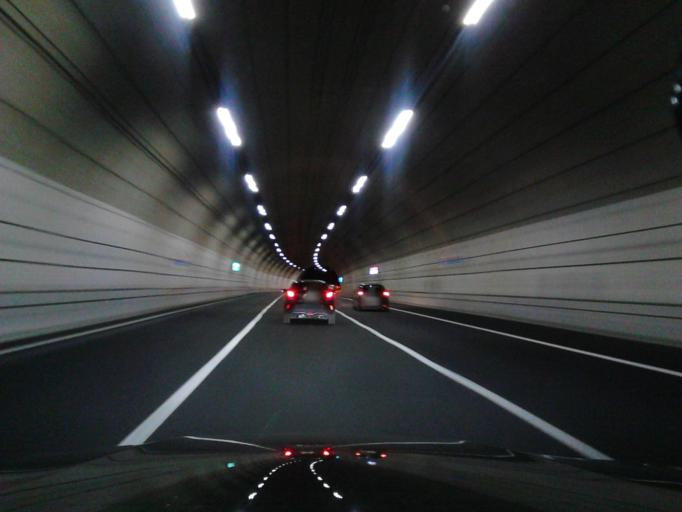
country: IT
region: The Marches
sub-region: Provincia di Ancona
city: Falconara Marittima
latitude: 43.5938
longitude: 13.3775
